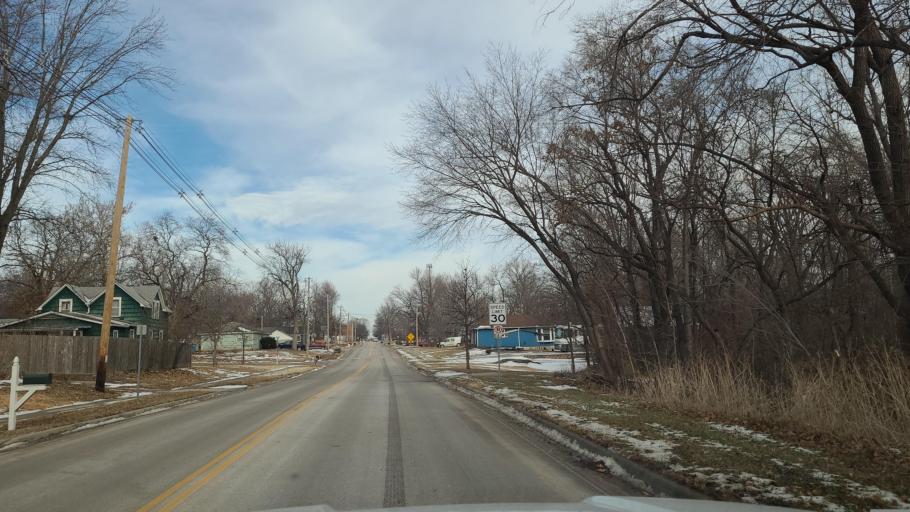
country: US
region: Kansas
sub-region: Douglas County
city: Baldwin City
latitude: 38.7709
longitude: -95.1860
